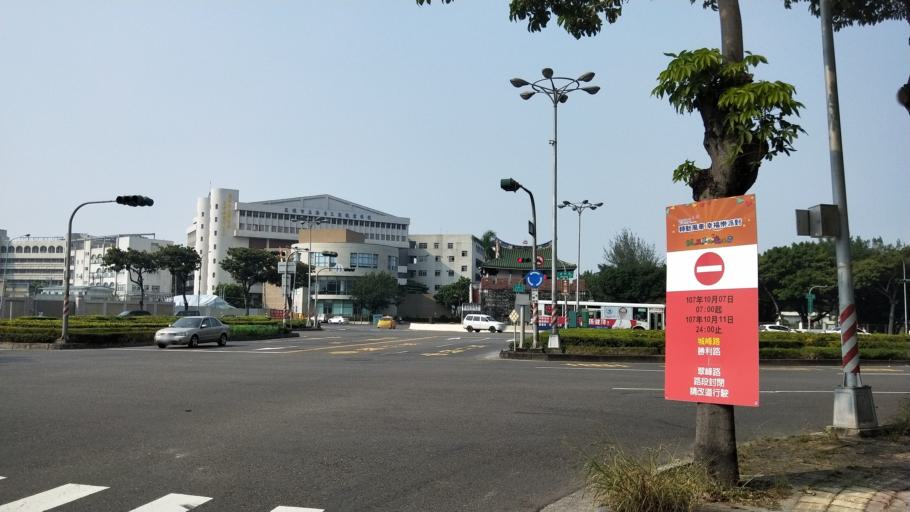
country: TW
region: Kaohsiung
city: Kaohsiung
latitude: 22.6715
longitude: 120.2867
